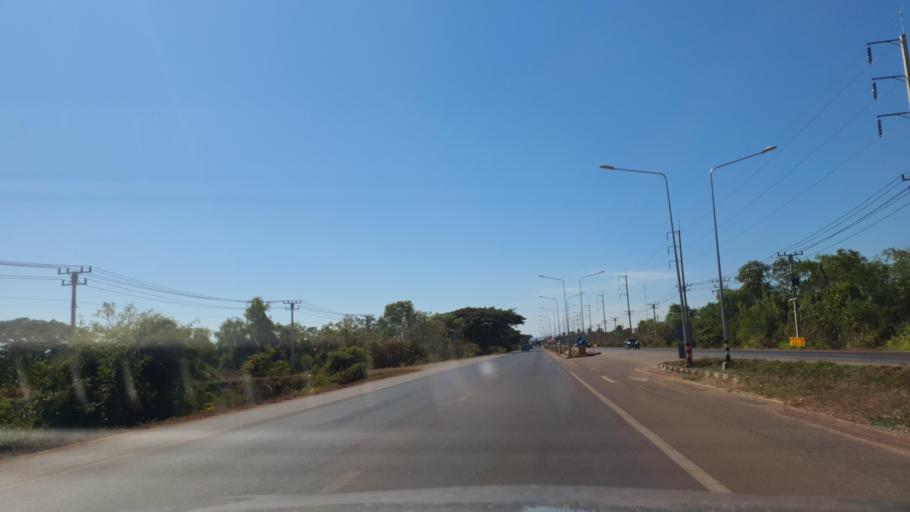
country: TH
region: Sakon Nakhon
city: Sakon Nakhon
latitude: 17.2575
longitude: 104.1159
